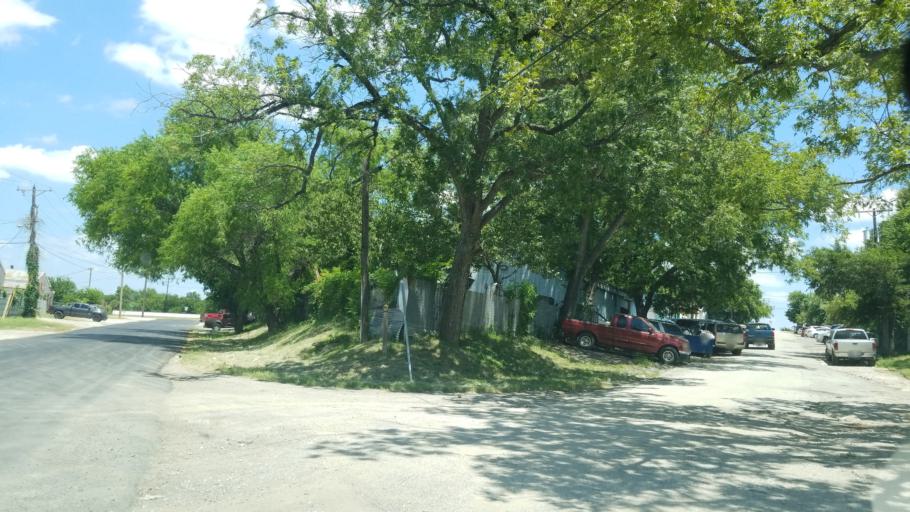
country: US
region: Texas
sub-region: Dallas County
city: Hutchins
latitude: 32.7344
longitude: -96.7168
